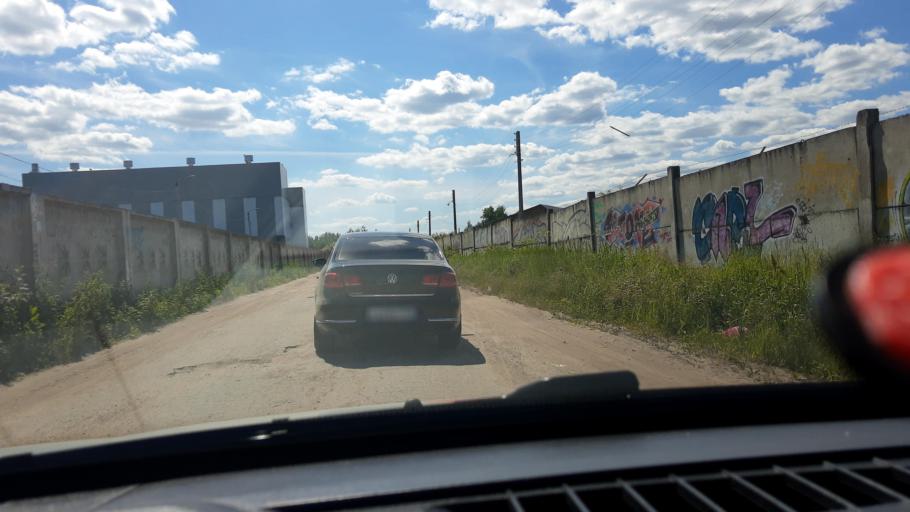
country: RU
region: Nizjnij Novgorod
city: Gorbatovka
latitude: 56.3043
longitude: 43.8134
